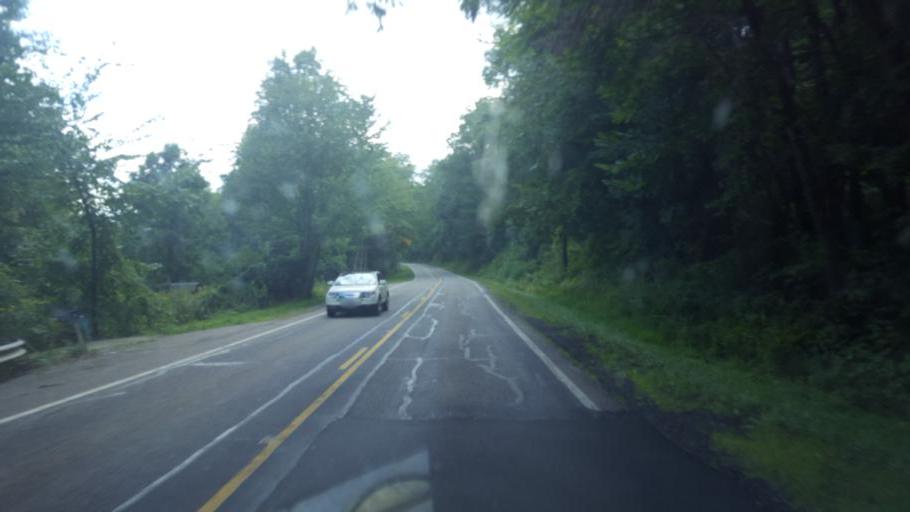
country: US
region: Ohio
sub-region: Tuscarawas County
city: Dover
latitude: 40.5548
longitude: -81.4187
